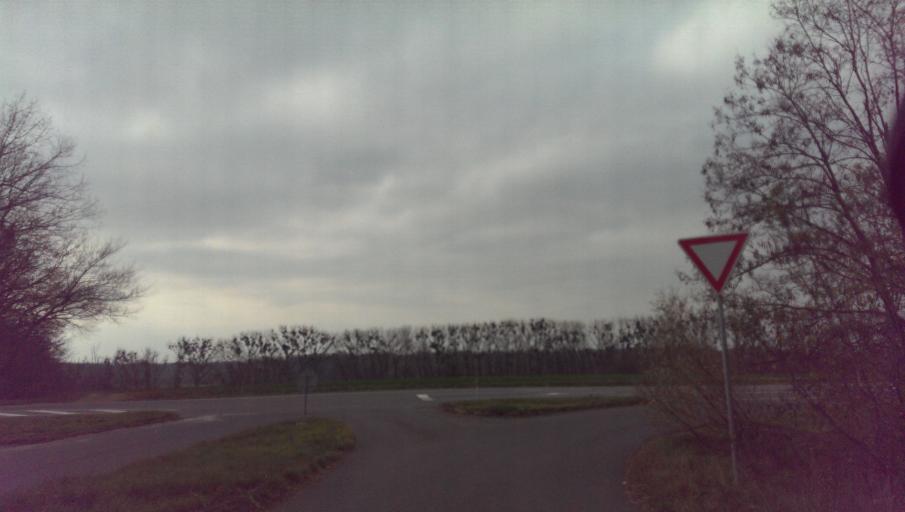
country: CZ
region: Zlin
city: Tlumacov
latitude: 49.2691
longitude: 17.4913
